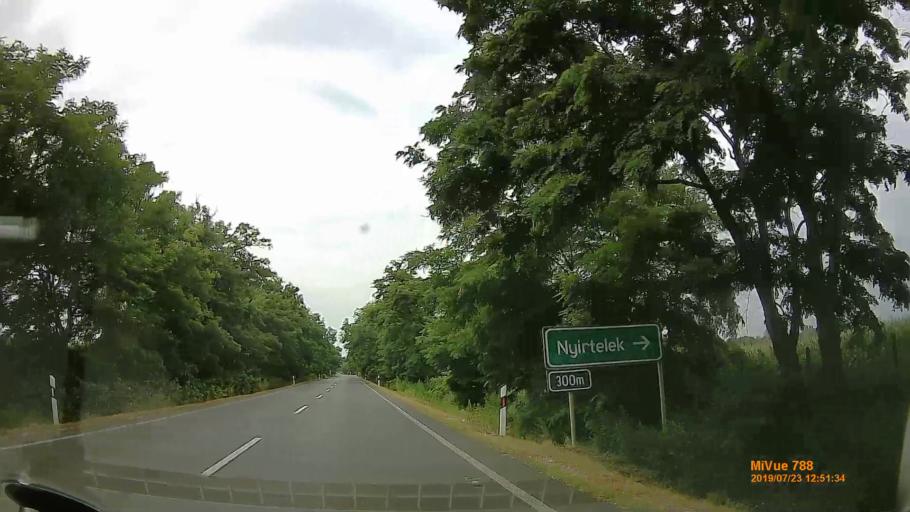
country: HU
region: Szabolcs-Szatmar-Bereg
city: Nagycserkesz
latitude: 47.9595
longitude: 21.5838
